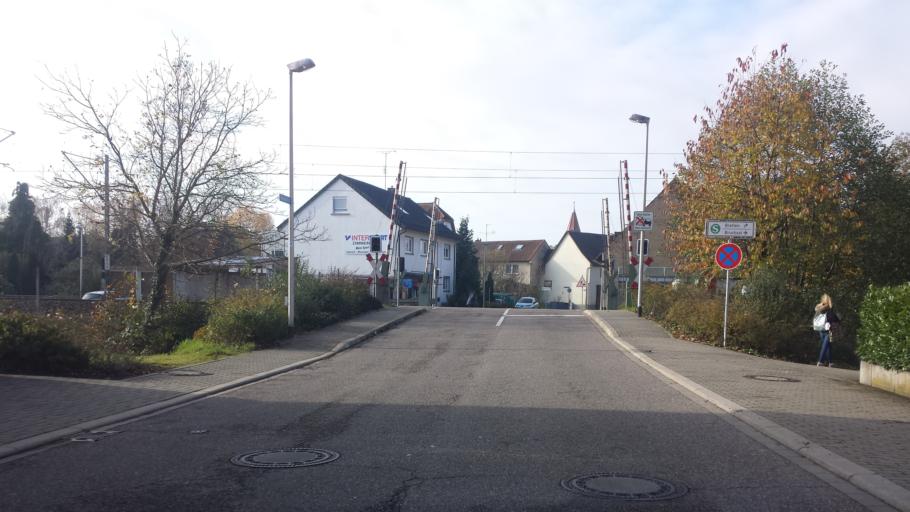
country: DE
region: Baden-Wuerttemberg
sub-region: Karlsruhe Region
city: Gondelsheim
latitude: 49.1013
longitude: 8.6503
